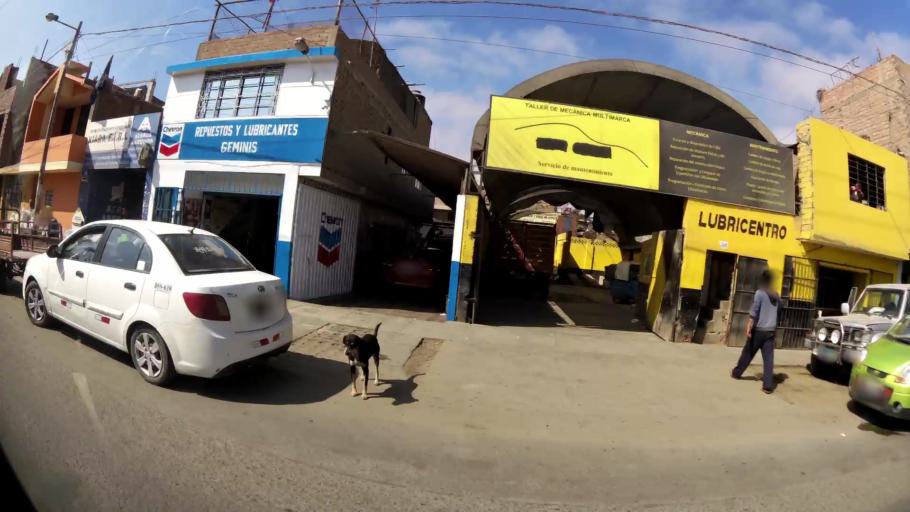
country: PE
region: Ica
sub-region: Provincia de Ica
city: Ica
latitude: -14.0710
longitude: -75.7227
